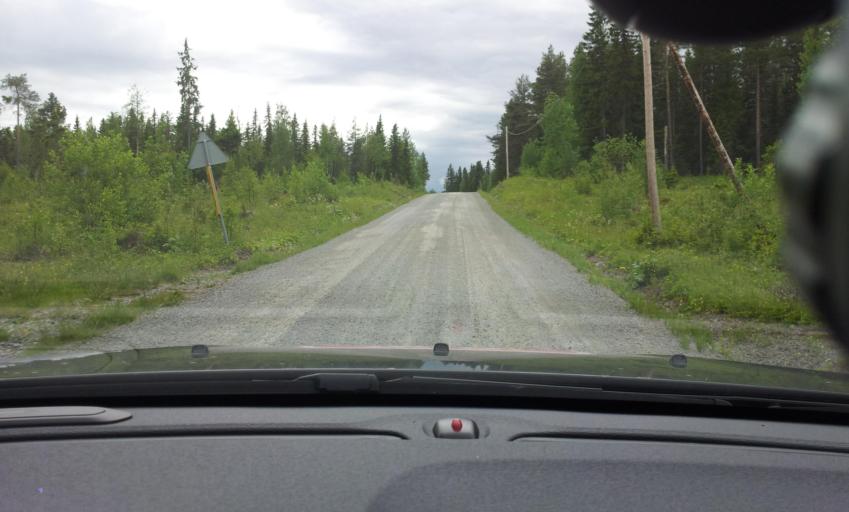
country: SE
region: Jaemtland
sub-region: OEstersunds Kommun
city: Brunflo
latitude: 62.9895
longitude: 14.7173
